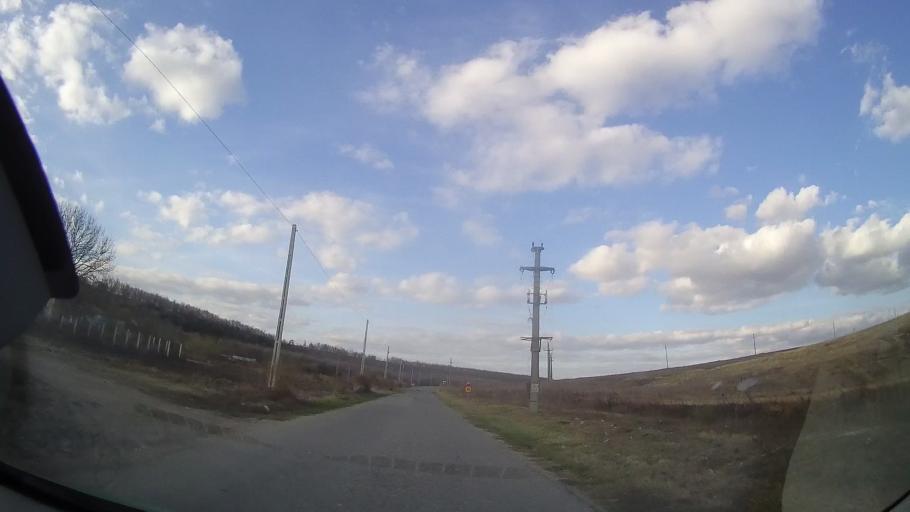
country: RO
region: Constanta
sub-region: Comuna Cerchezu
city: Cerchezu
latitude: 43.8281
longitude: 28.0975
